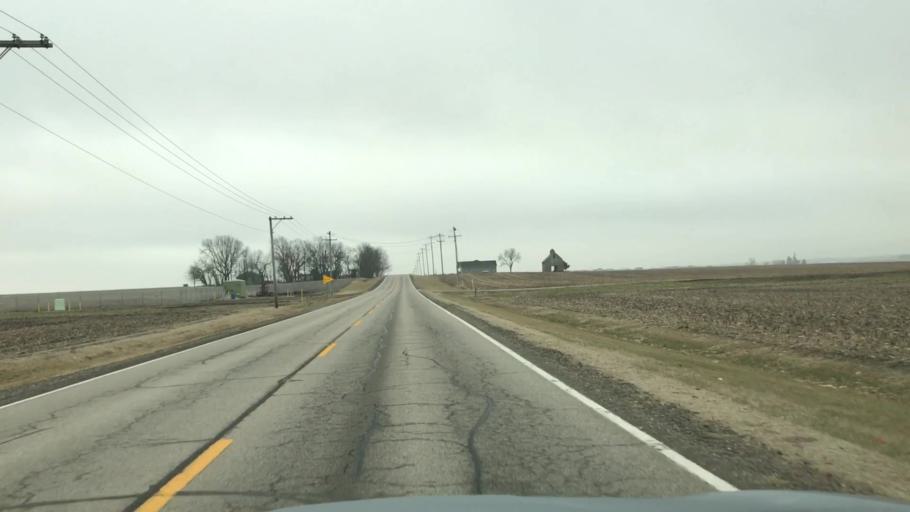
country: US
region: Illinois
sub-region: McLean County
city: Hudson
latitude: 40.5737
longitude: -88.9447
